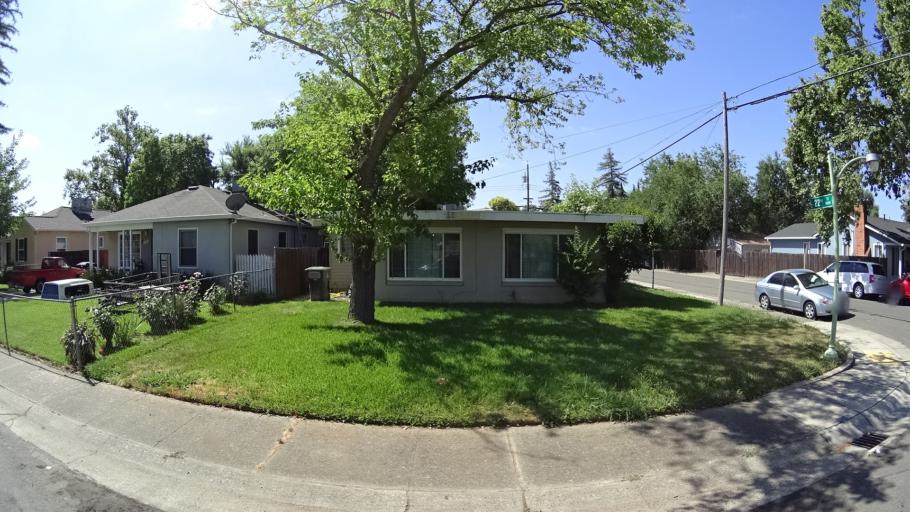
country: US
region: California
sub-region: Sacramento County
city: Sacramento
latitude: 38.5368
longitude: -121.4882
